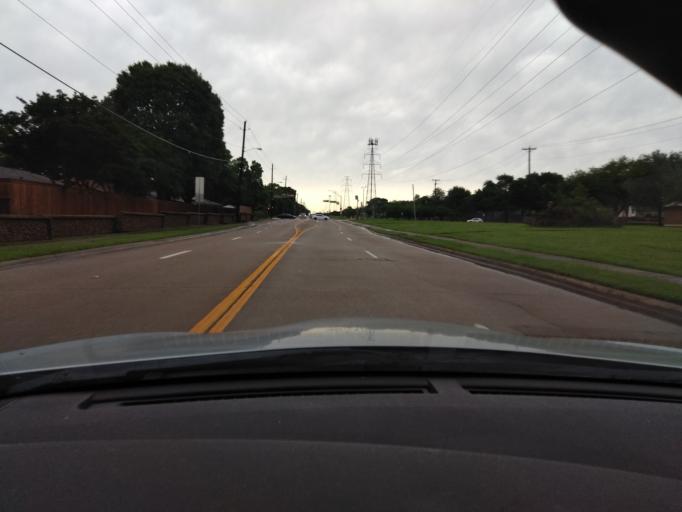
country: US
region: Texas
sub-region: Dallas County
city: Richardson
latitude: 32.9607
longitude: -96.7786
